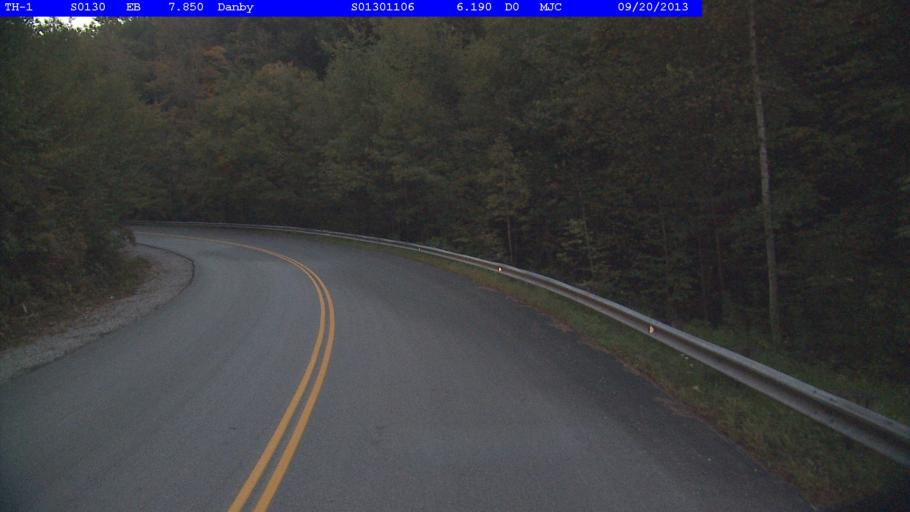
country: US
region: Vermont
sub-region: Bennington County
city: Manchester Center
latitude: 43.3410
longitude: -73.0295
